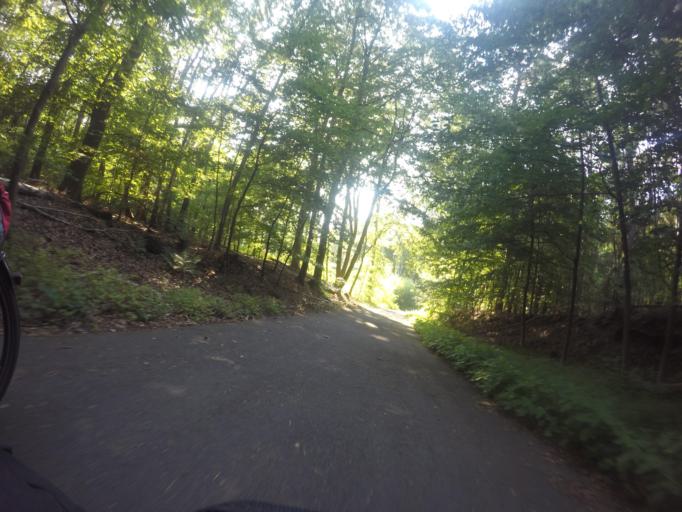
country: DE
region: Lower Saxony
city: Dahlenburg
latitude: 53.2051
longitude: 10.7294
